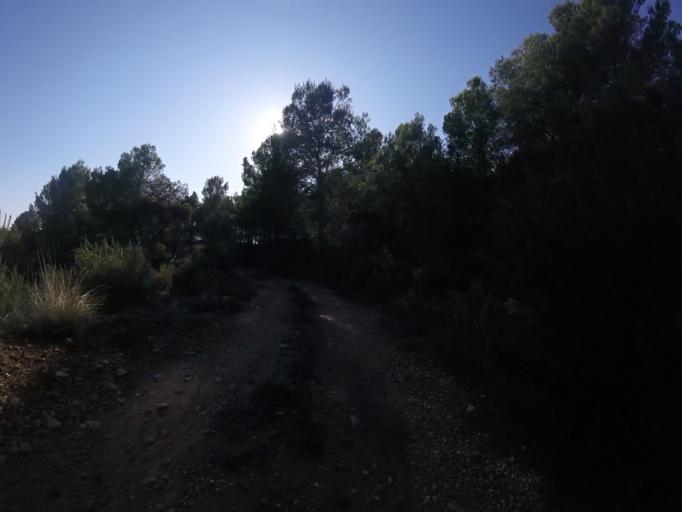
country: ES
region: Valencia
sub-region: Provincia de Castello
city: Sarratella
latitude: 40.2846
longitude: 0.0652
